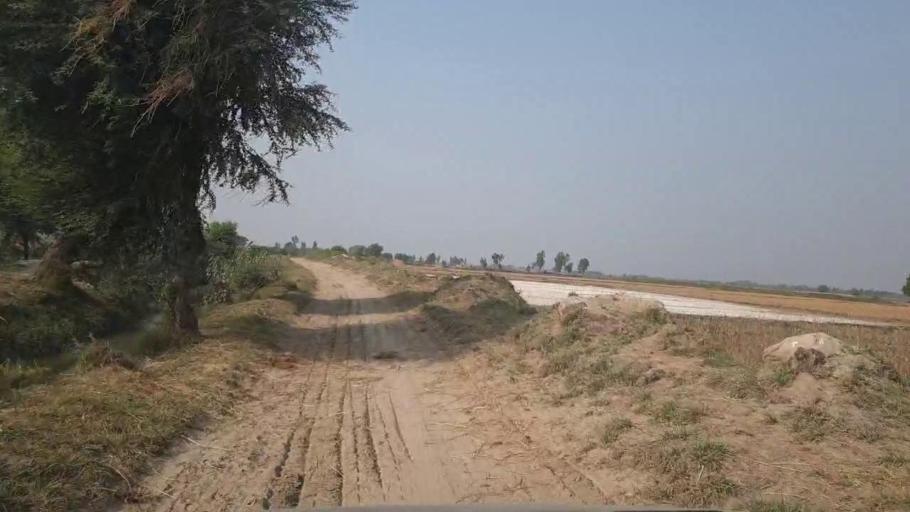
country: PK
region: Sindh
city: Tando Muhammad Khan
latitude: 25.0722
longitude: 68.3558
